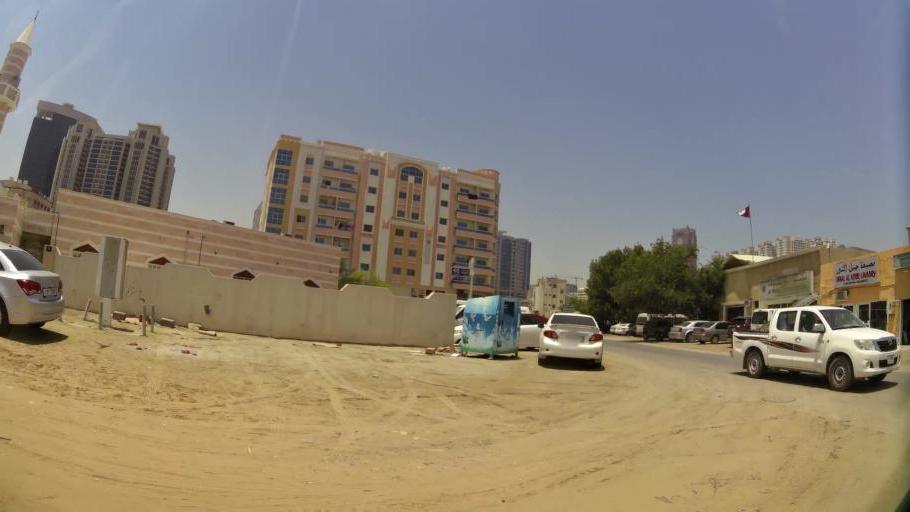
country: AE
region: Ajman
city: Ajman
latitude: 25.3958
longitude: 55.4387
